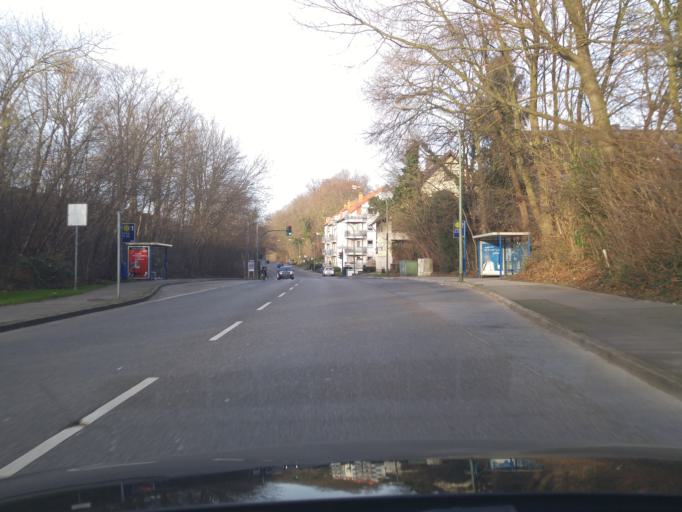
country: DE
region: North Rhine-Westphalia
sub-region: Regierungsbezirk Dusseldorf
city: Velbert
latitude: 51.3998
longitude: 7.0861
